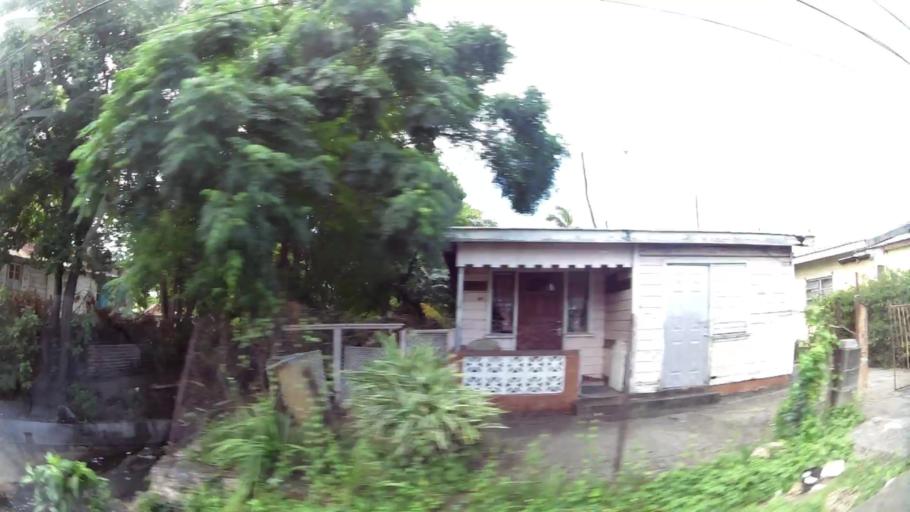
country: AG
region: Saint John
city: Saint John's
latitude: 17.1118
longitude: -61.8447
